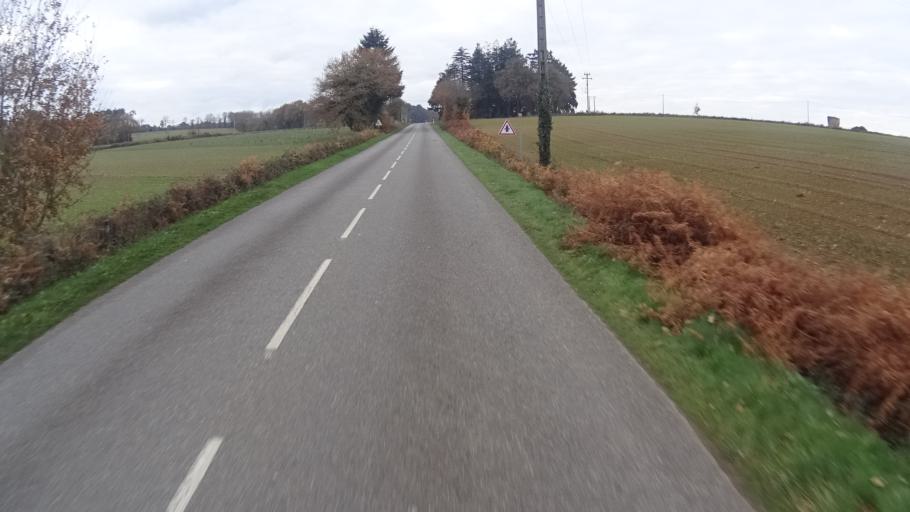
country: FR
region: Pays de la Loire
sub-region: Departement de la Loire-Atlantique
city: Avessac
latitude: 47.6550
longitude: -1.9553
